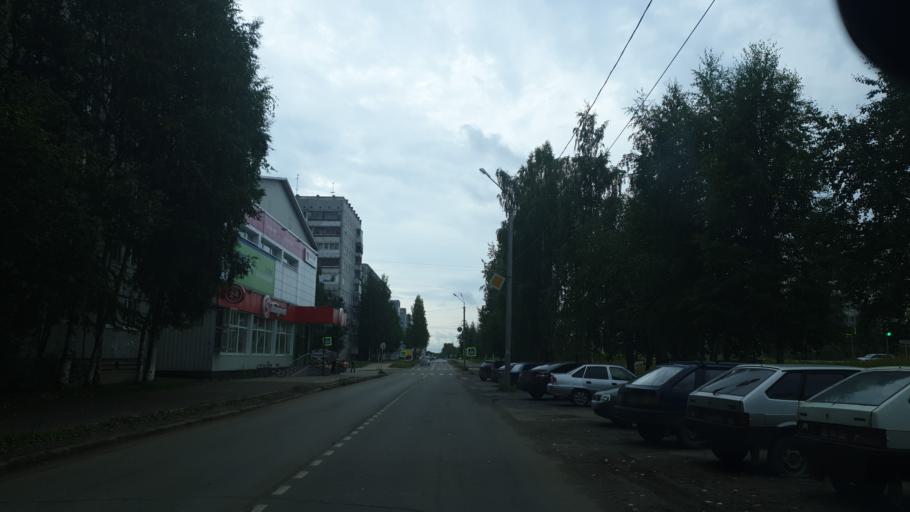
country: RU
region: Komi Republic
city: Ezhva
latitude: 61.7878
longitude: 50.7443
